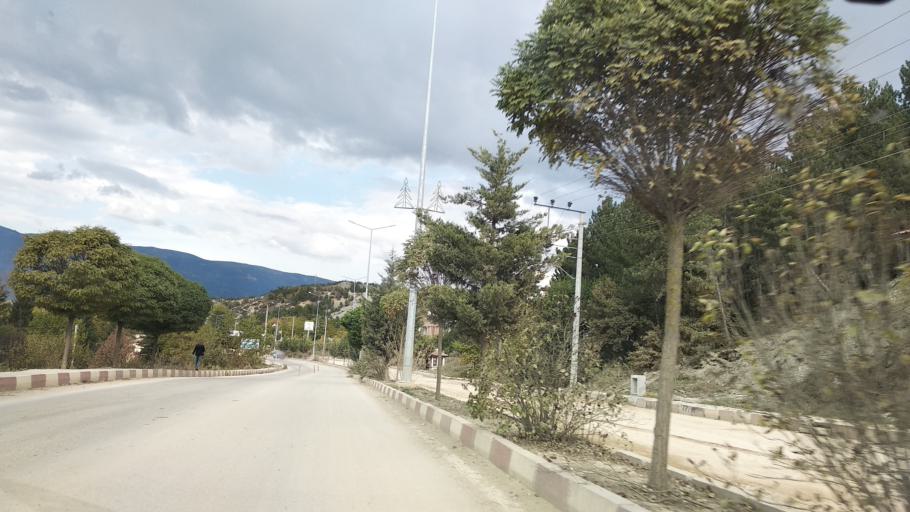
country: TR
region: Bolu
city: Mudurnu
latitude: 40.4762
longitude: 31.2104
